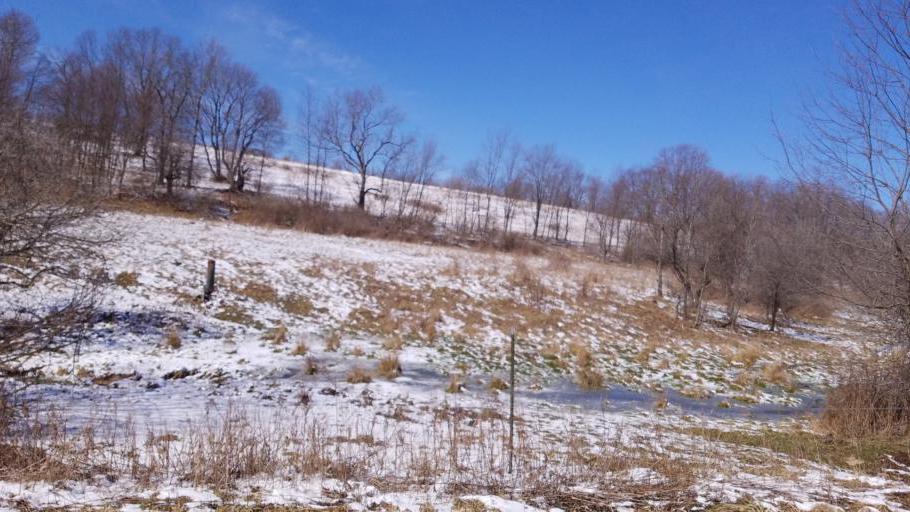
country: US
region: New York
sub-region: Allegany County
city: Andover
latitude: 41.9324
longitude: -77.7763
